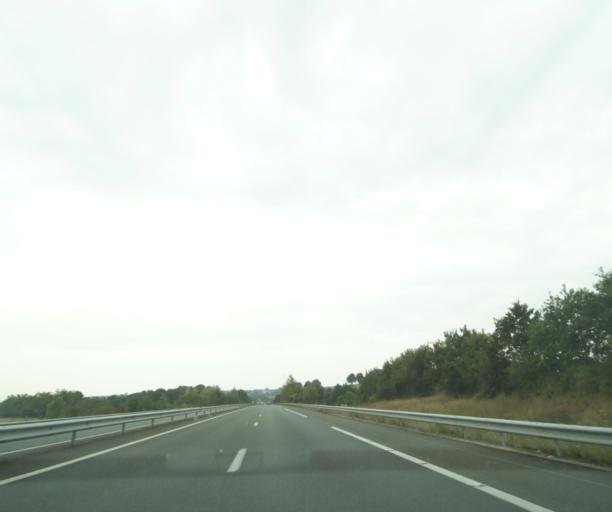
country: FR
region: Pays de la Loire
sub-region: Departement de la Vendee
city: Bournezeau
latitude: 46.6739
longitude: -1.1563
